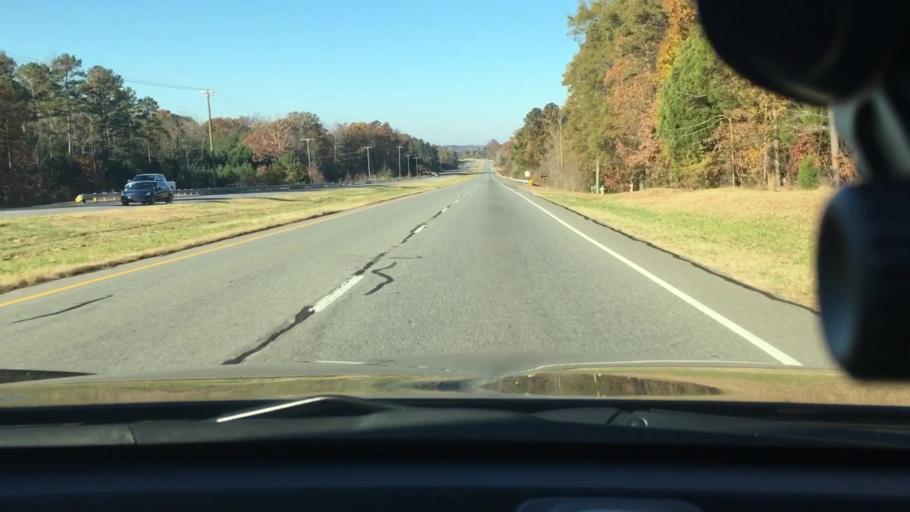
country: US
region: North Carolina
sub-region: Cabarrus County
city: Mount Pleasant
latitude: 35.3861
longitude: -80.5045
